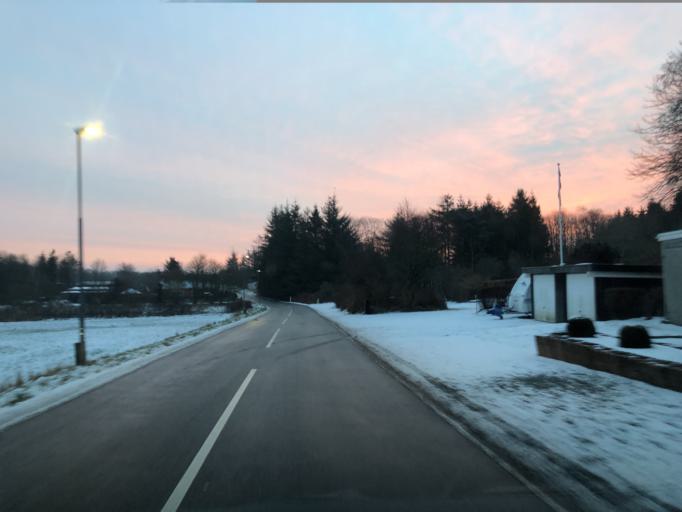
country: DK
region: Central Jutland
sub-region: Holstebro Kommune
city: Ulfborg
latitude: 56.2011
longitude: 8.4297
